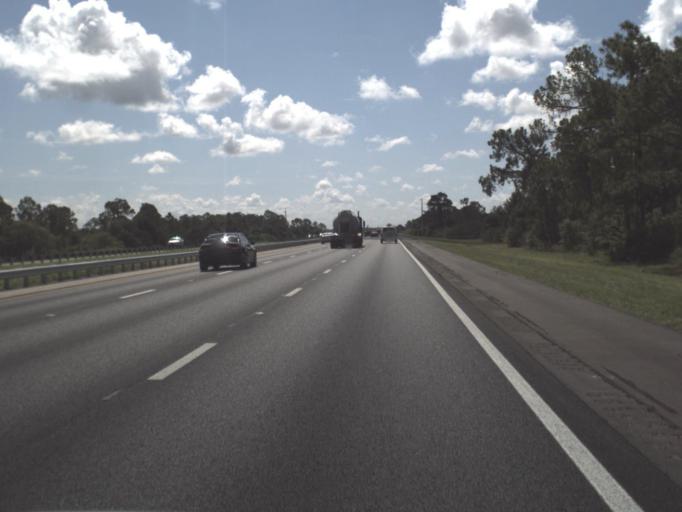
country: US
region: Florida
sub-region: Lee County
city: Suncoast Estates
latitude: 26.7348
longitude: -81.8452
